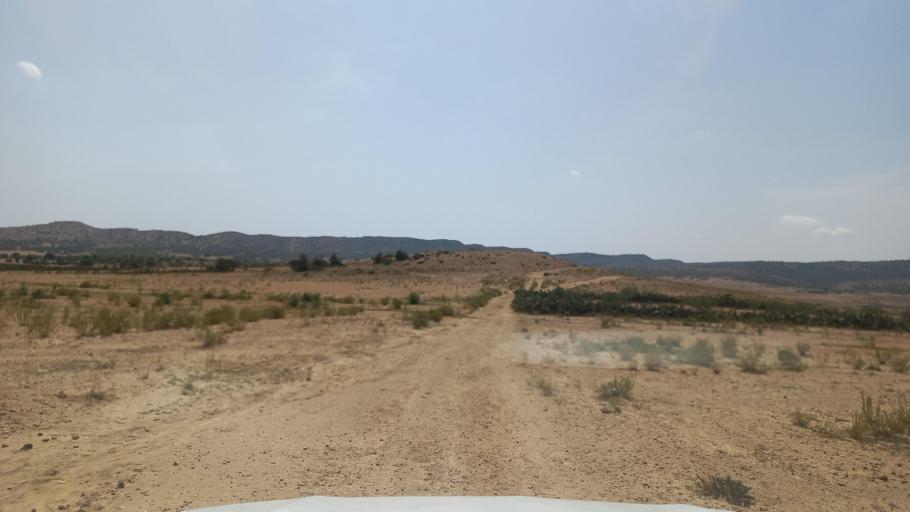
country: TN
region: Al Qasrayn
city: Sbiba
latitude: 35.3999
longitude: 8.9740
